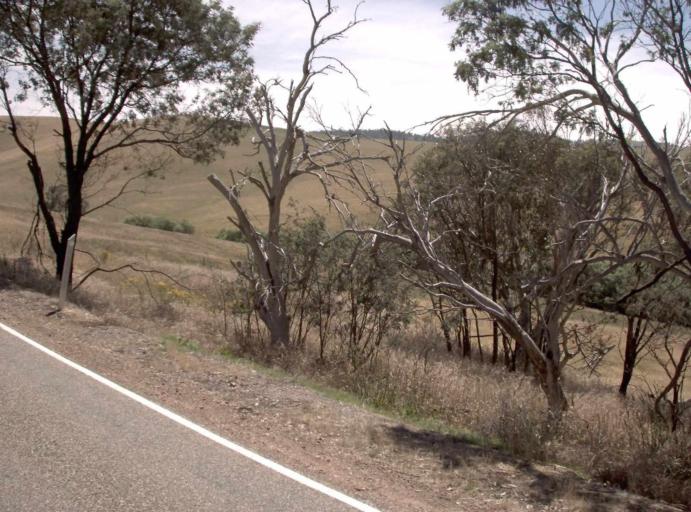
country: AU
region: Victoria
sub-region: Alpine
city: Mount Beauty
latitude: -37.0605
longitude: 147.6176
